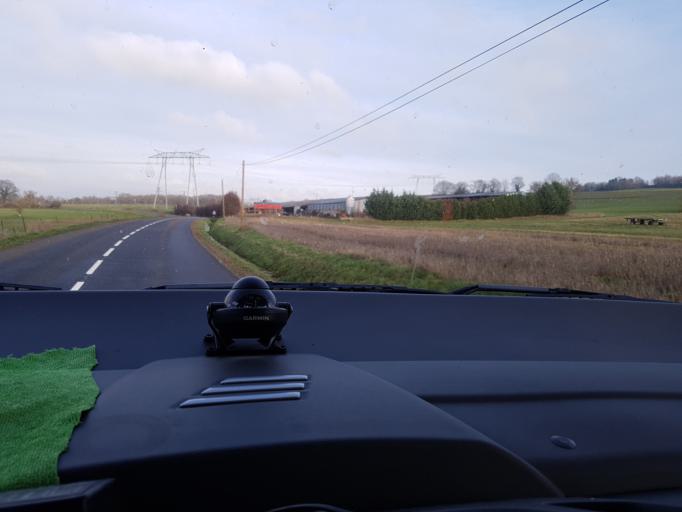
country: FR
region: Champagne-Ardenne
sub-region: Departement des Ardennes
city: Tournes
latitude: 49.7529
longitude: 4.6185
